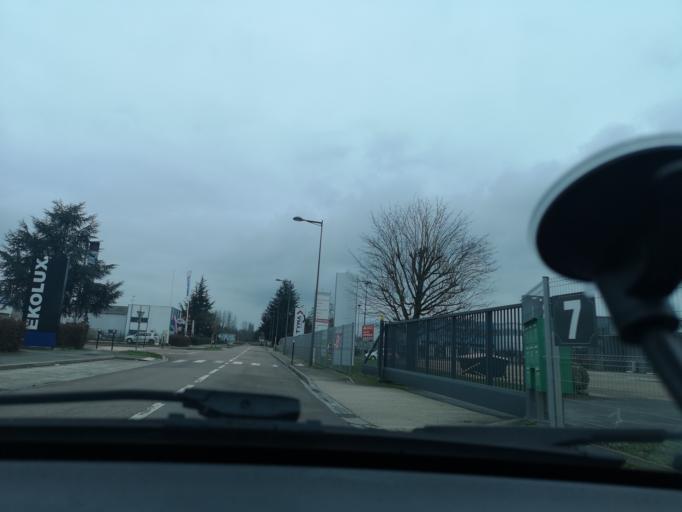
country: FR
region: Bourgogne
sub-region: Departement de Saone-et-Loire
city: Chatenoy-le-Royal
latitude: 46.7968
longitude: 4.8285
